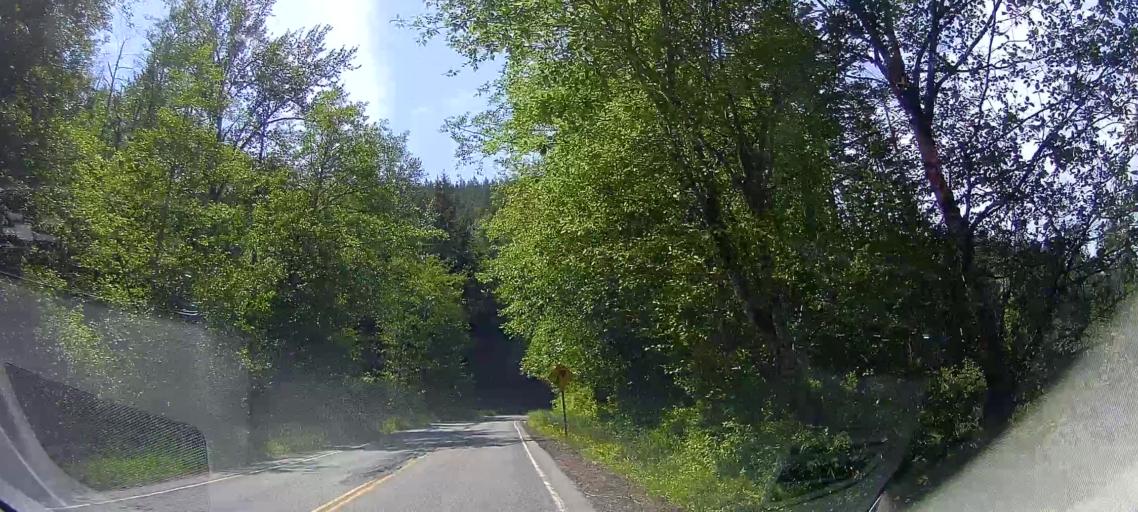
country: US
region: Washington
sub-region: Skagit County
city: Mount Vernon
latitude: 48.3980
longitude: -122.2982
